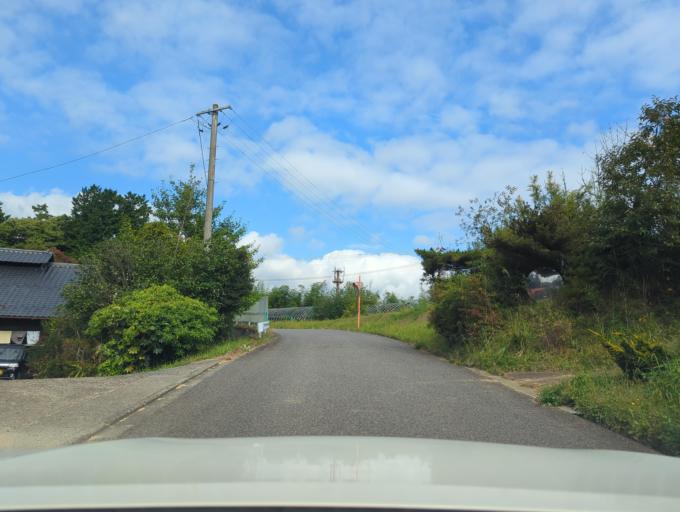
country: JP
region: Fukushima
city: Motomiya
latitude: 37.5284
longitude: 140.3348
